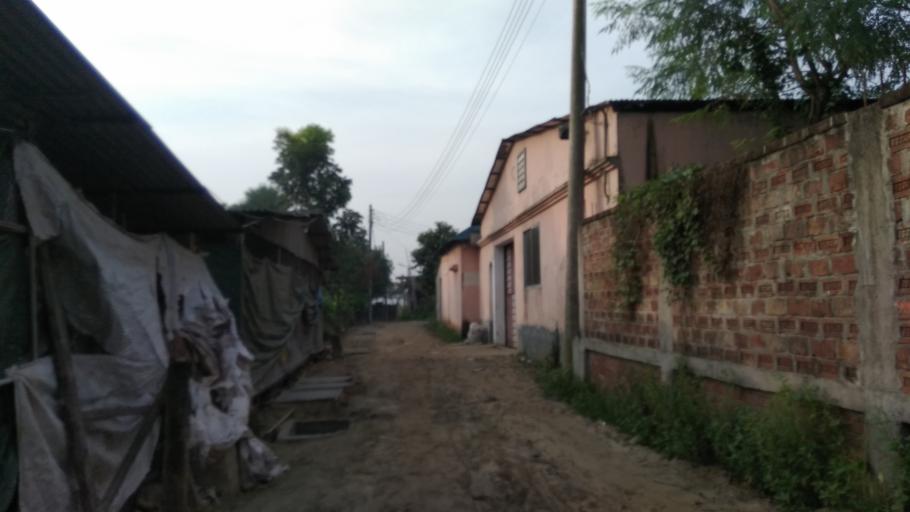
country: BD
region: Dhaka
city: Tungi
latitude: 23.8523
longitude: 90.4429
